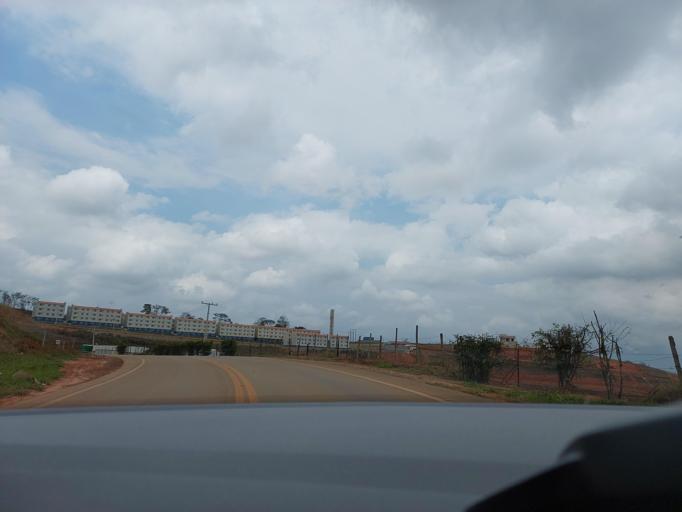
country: BR
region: Minas Gerais
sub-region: Ponte Nova
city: Ponte Nova
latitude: -20.3934
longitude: -42.8715
